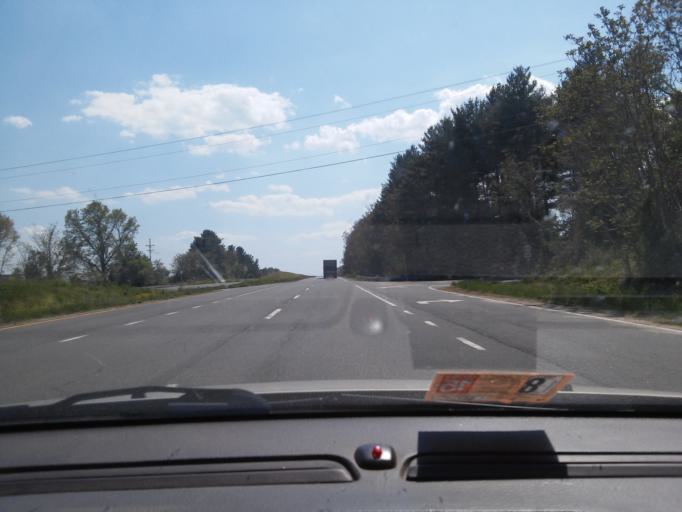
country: US
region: Virginia
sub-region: Rappahannock County
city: Washington
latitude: 38.7085
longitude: -78.1561
